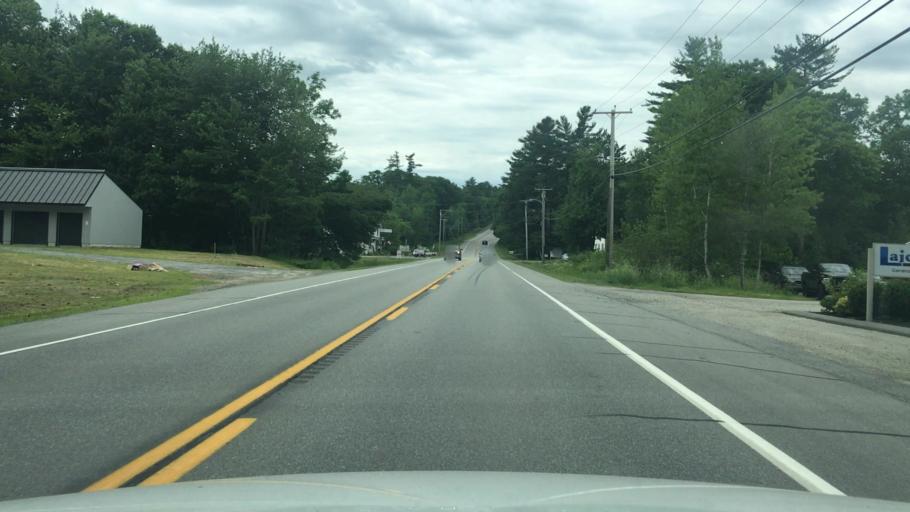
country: US
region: Maine
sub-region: Kennebec County
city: Windsor
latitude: 44.3399
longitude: -69.6670
